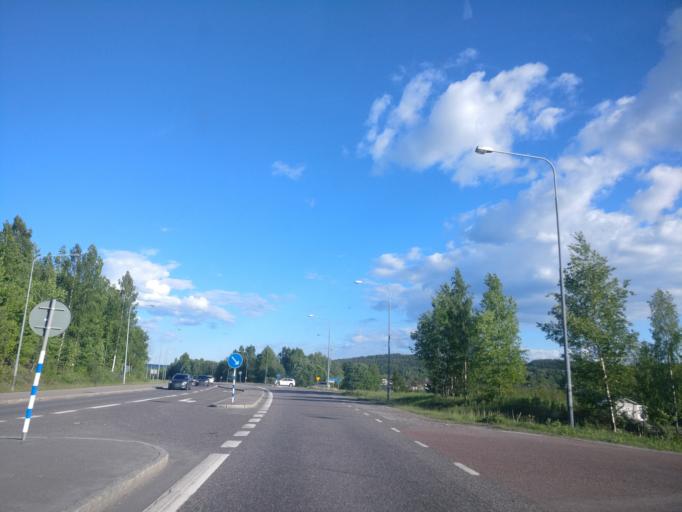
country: SE
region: Vaesternorrland
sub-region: Sundsvalls Kommun
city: Sundsbruk
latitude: 62.4470
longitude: 17.3445
